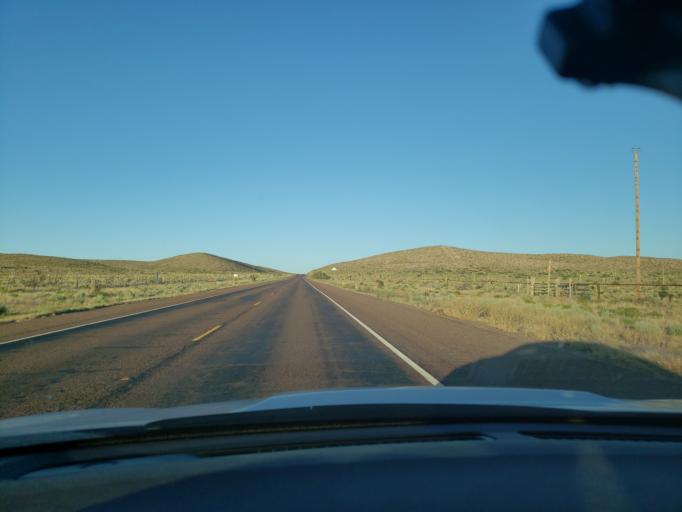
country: US
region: Texas
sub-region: El Paso County
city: Homestead Meadows South
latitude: 31.8267
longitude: -105.9015
